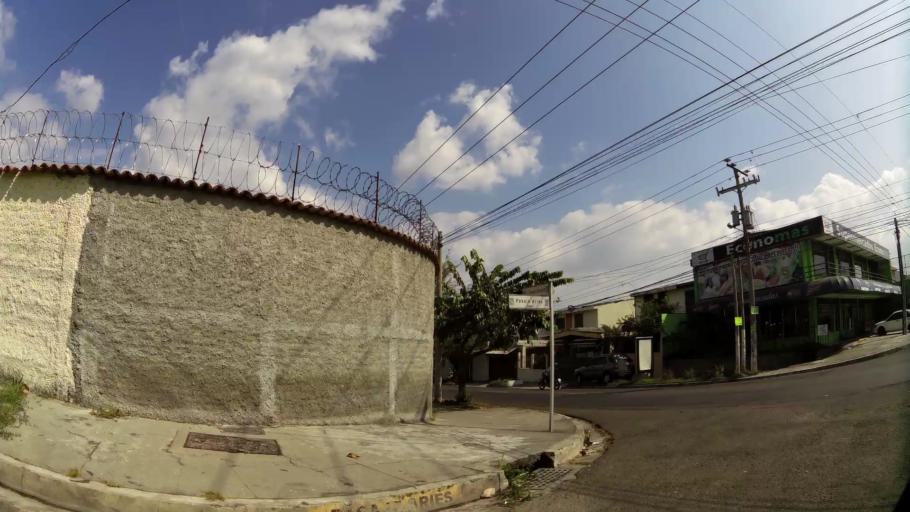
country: SV
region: San Salvador
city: Mejicanos
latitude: 13.7232
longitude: -89.2175
